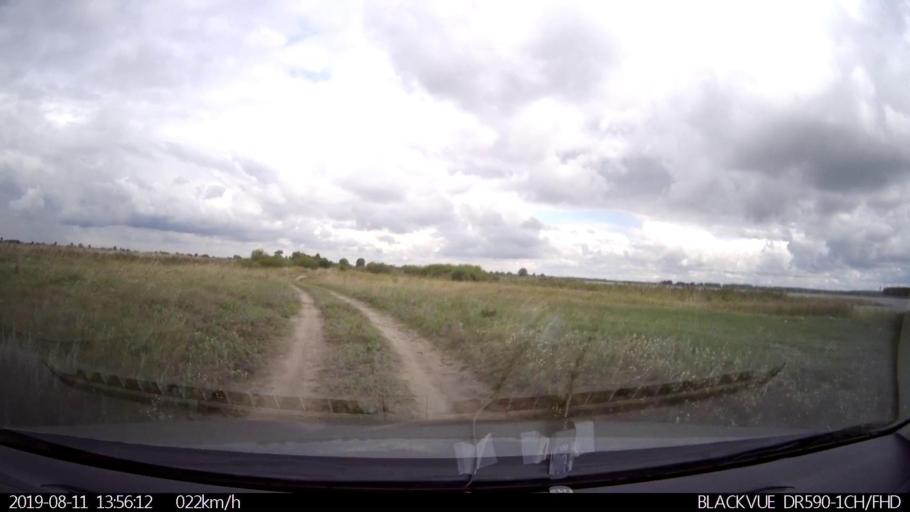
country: RU
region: Ulyanovsk
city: Ignatovka
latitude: 53.8471
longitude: 47.5881
